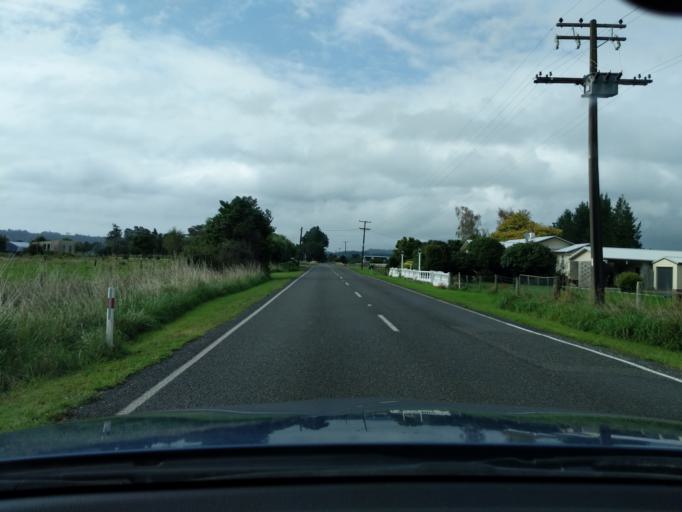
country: NZ
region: Tasman
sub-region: Tasman District
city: Takaka
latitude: -40.6655
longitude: 172.6511
